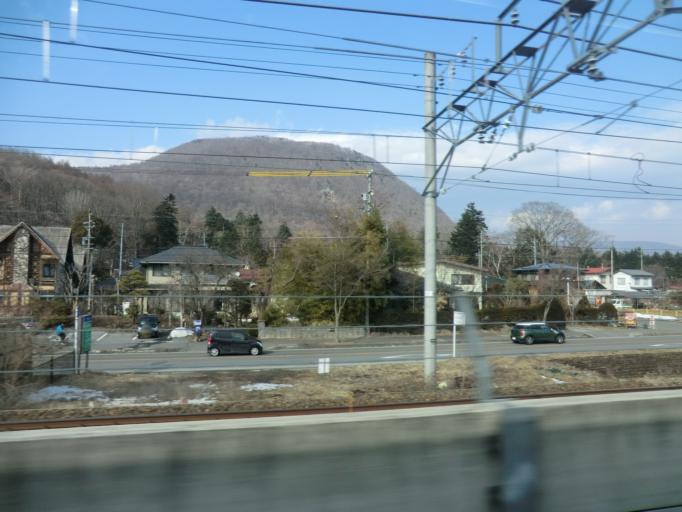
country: JP
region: Nagano
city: Komoro
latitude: 36.3437
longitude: 138.6117
